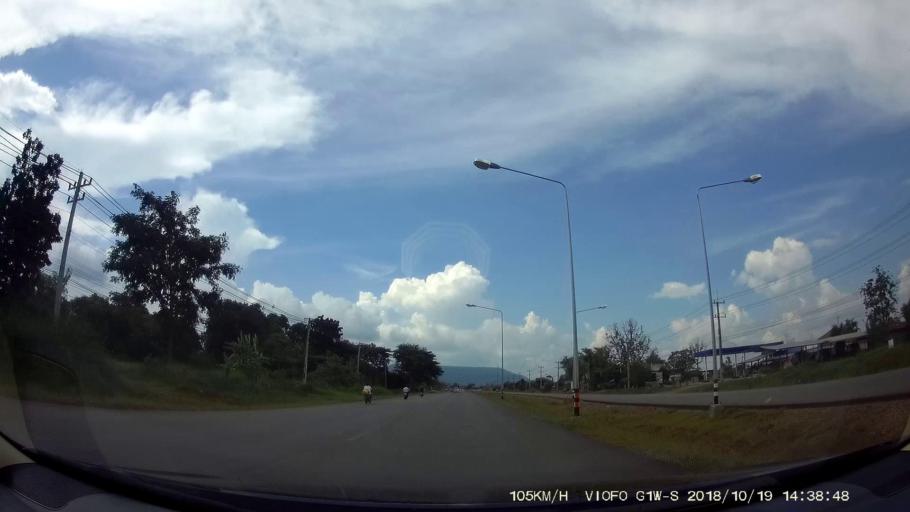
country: TH
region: Chaiyaphum
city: Kaeng Khro
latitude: 16.2182
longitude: 102.1989
